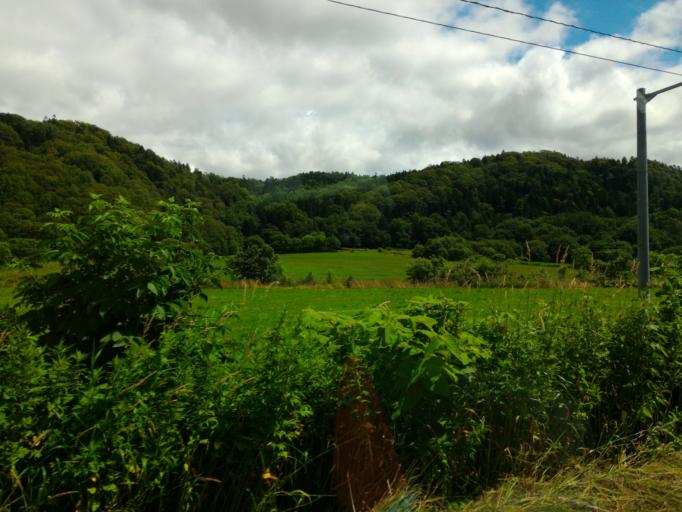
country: JP
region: Hokkaido
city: Nayoro
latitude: 44.6146
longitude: 142.3066
